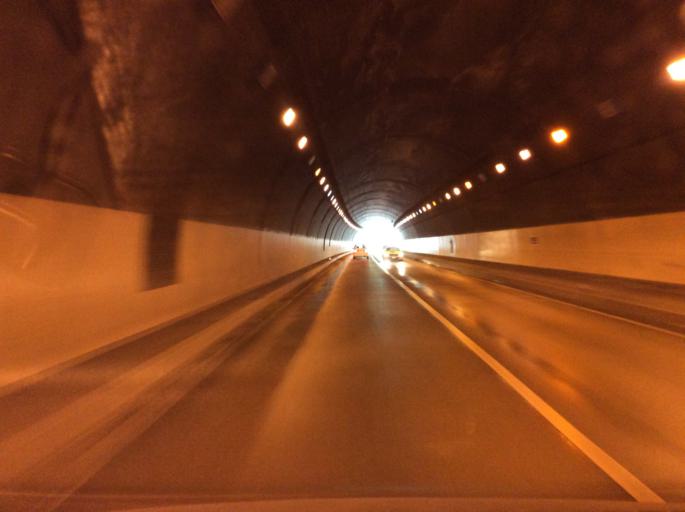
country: JP
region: Fukushima
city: Iwaki
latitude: 37.0296
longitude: 140.8803
